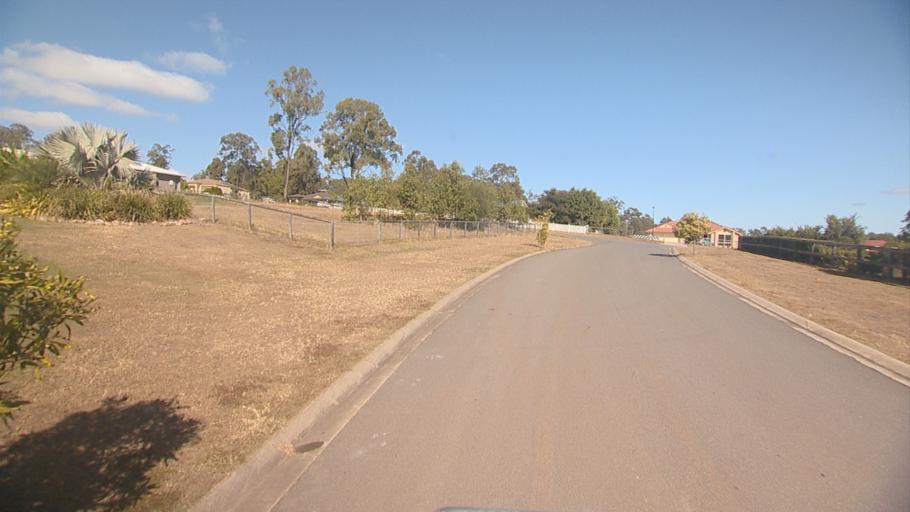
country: AU
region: Queensland
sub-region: Logan
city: Cedar Vale
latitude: -27.8906
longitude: 153.0000
